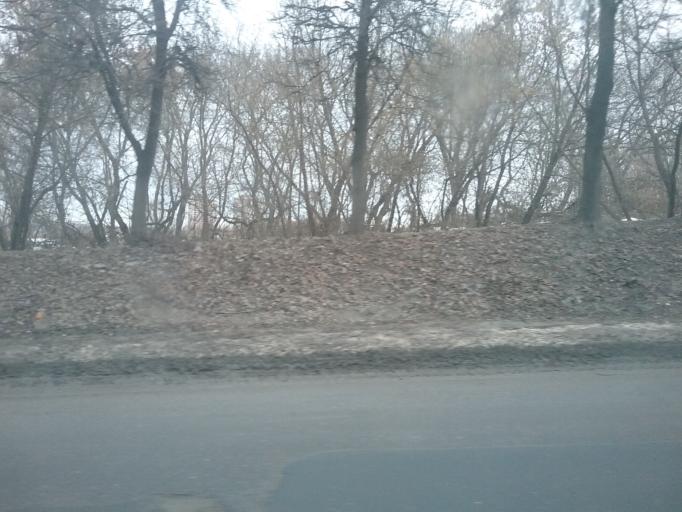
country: RU
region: Tula
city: Tula
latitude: 54.1691
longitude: 37.6406
